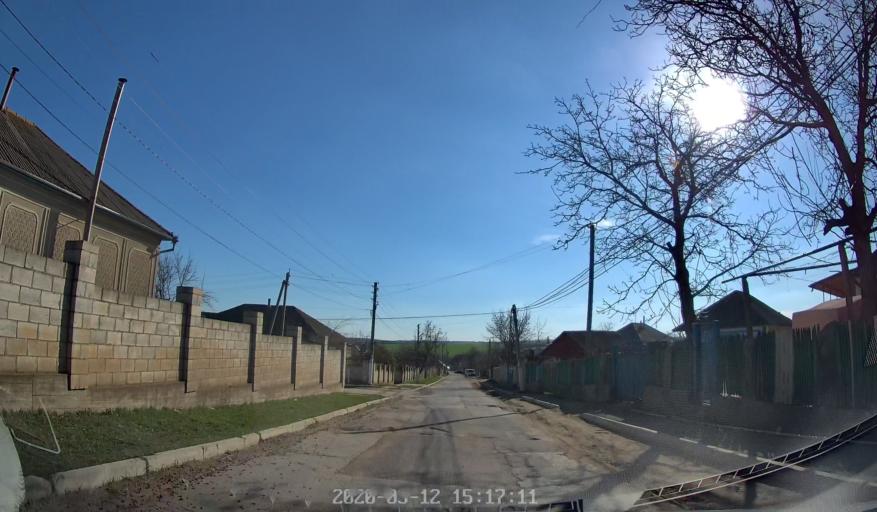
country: MD
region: Chisinau
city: Ciorescu
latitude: 47.2221
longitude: 28.9359
